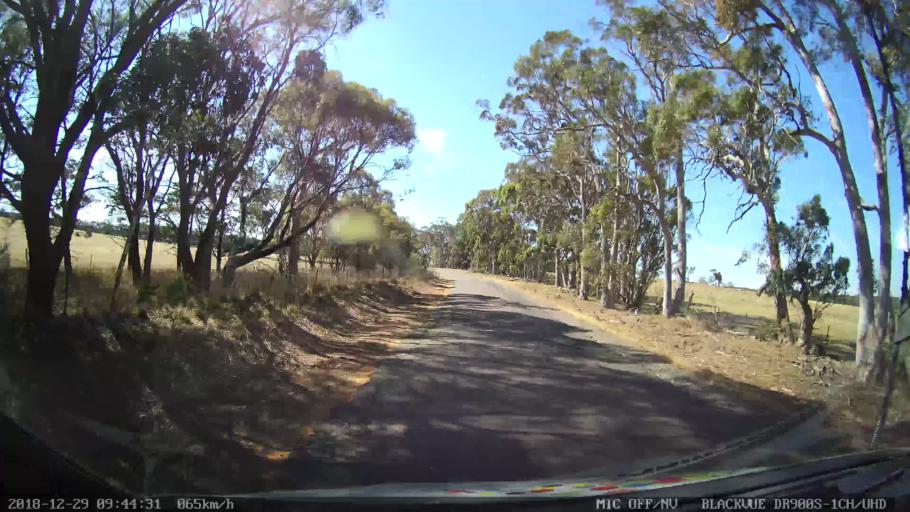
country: AU
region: New South Wales
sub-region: Upper Lachlan Shire
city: Crookwell
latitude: -34.6899
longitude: 149.4268
